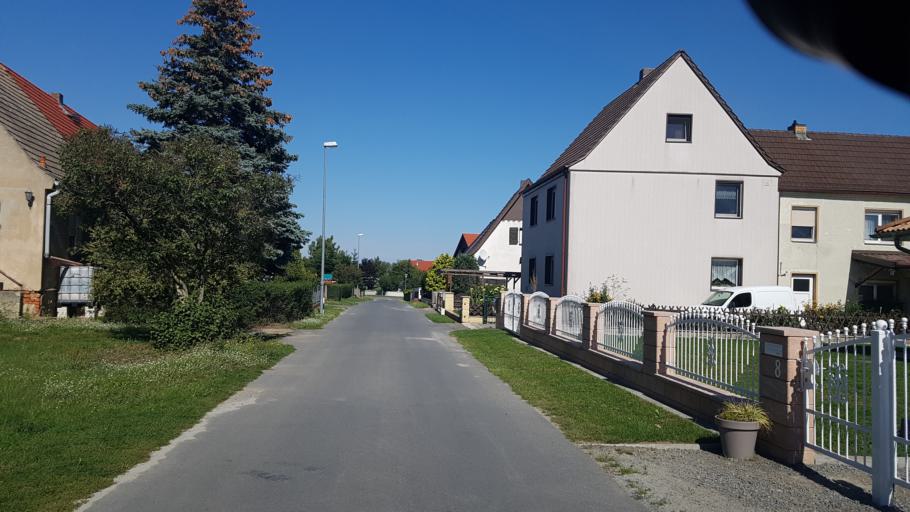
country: DE
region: Brandenburg
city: Hirschfeld
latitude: 51.3916
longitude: 13.6145
